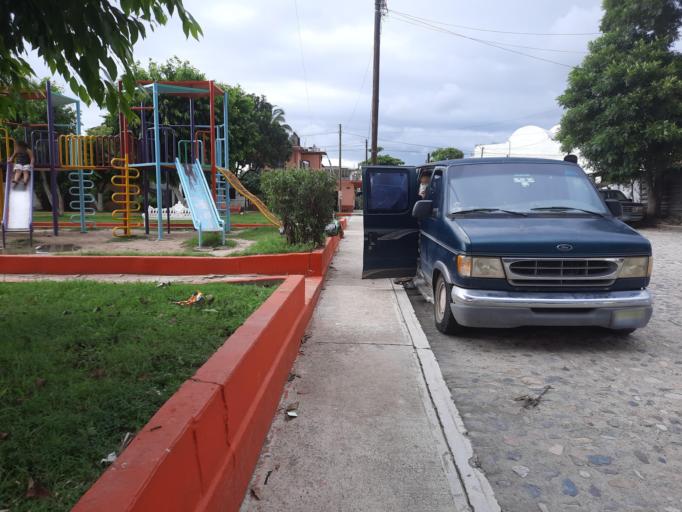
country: MX
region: Jalisco
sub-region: Puerto Vallarta
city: Puerto Vallarta
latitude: 20.6488
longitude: -105.1996
